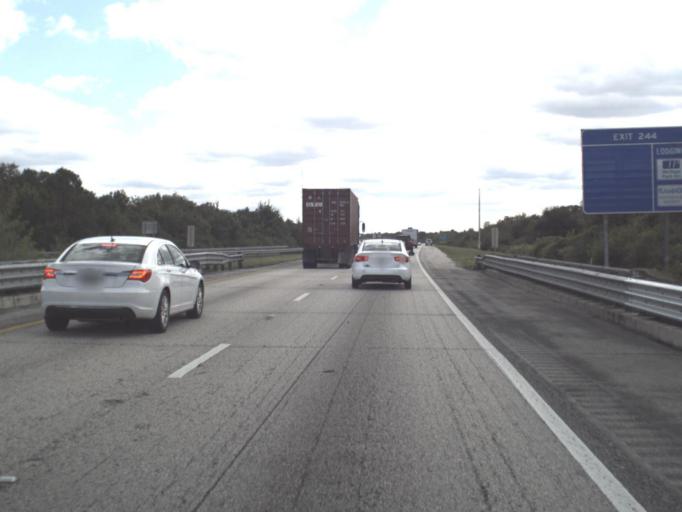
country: US
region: Florida
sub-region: Osceola County
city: Buenaventura Lakes
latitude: 28.3014
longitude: -81.3597
